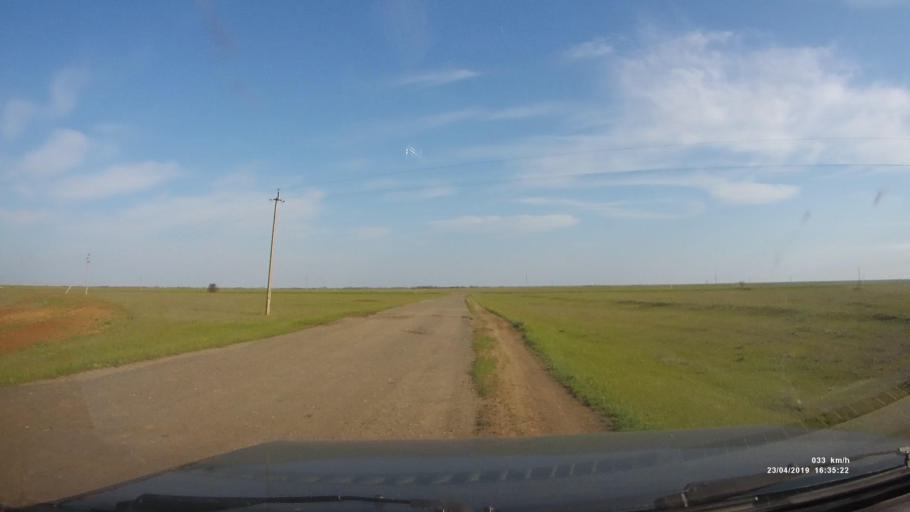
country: RU
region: Kalmykiya
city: Priyutnoye
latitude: 46.3311
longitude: 43.1371
